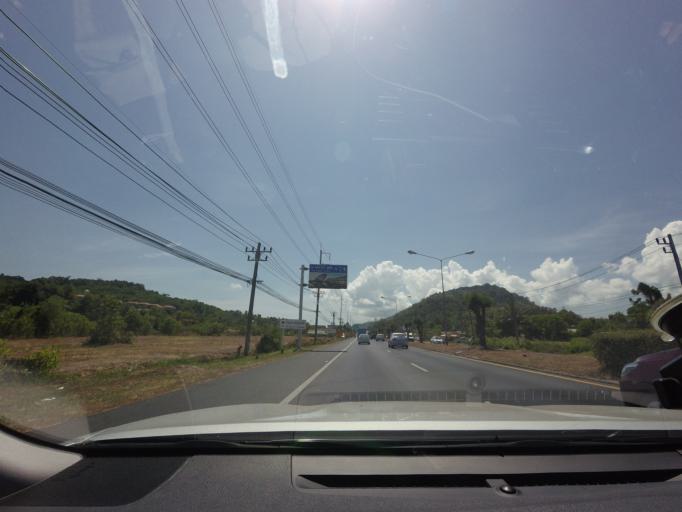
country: TH
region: Phuket
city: Ban Ko Kaeo
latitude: 7.9505
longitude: 98.3867
